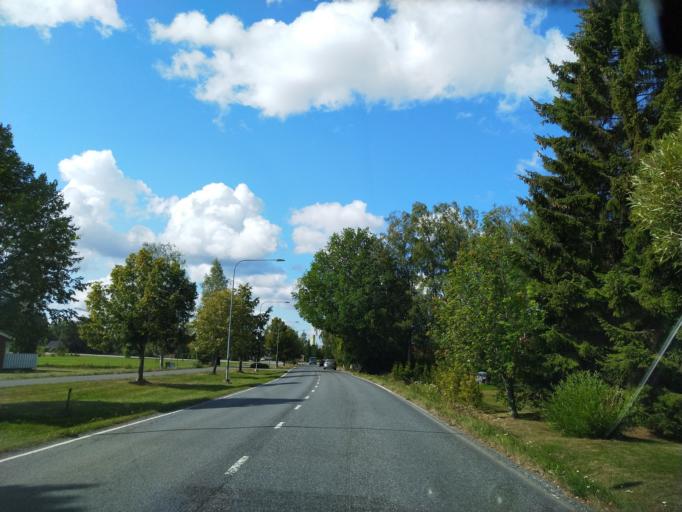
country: FI
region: Satakunta
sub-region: Pori
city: Huittinen
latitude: 61.1794
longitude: 22.7097
